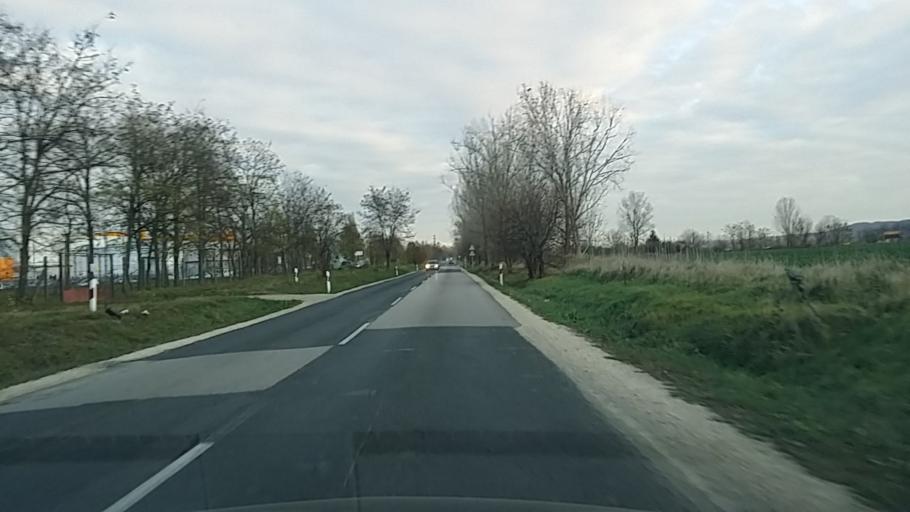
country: HU
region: Pest
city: Vac
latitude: 47.7711
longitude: 19.1637
